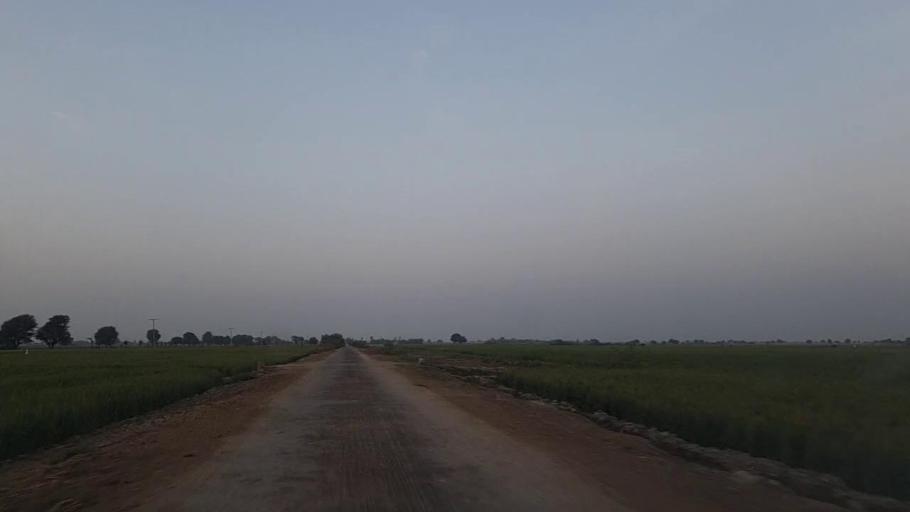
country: PK
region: Sindh
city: Naukot
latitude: 24.9881
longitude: 69.4245
